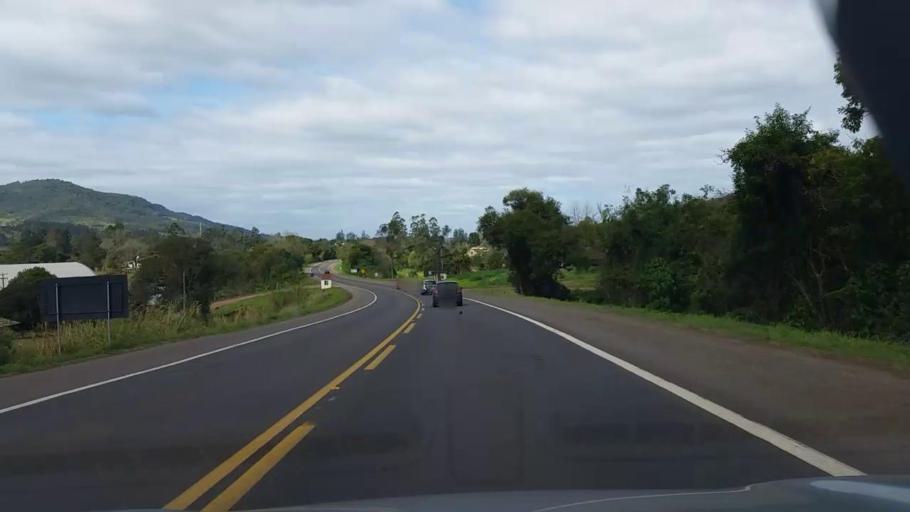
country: BR
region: Rio Grande do Sul
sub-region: Arroio Do Meio
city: Arroio do Meio
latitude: -29.3409
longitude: -52.0777
